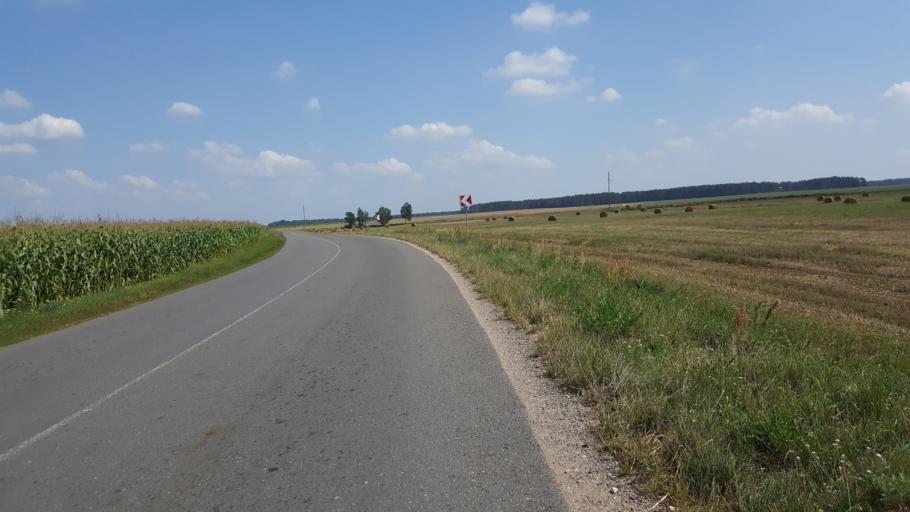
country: BY
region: Brest
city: Kamyanyuki
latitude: 52.4998
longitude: 23.6001
